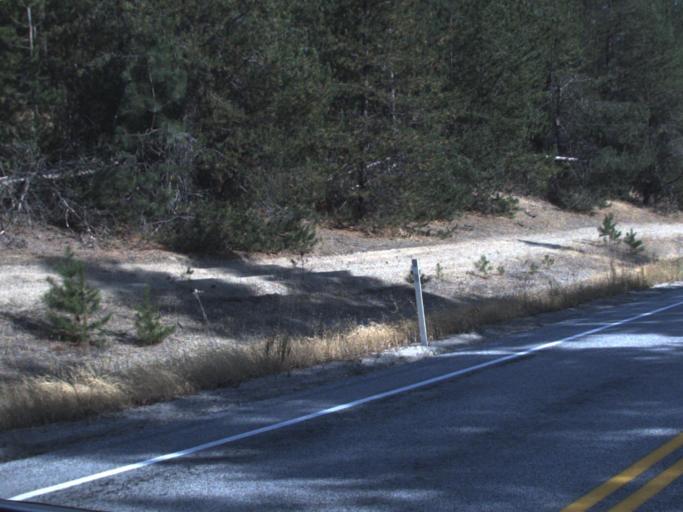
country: US
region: Washington
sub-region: Pend Oreille County
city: Newport
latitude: 48.1513
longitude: -117.3030
